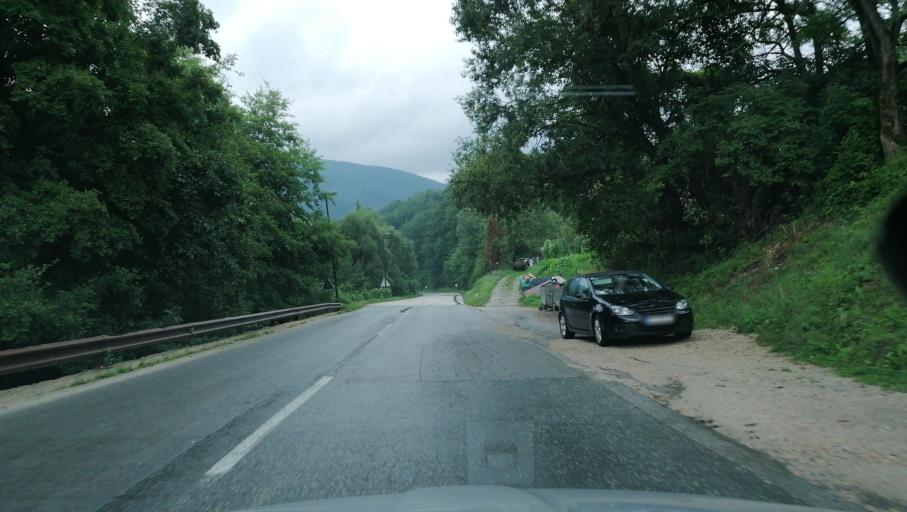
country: RS
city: Durici
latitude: 43.8002
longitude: 19.5060
